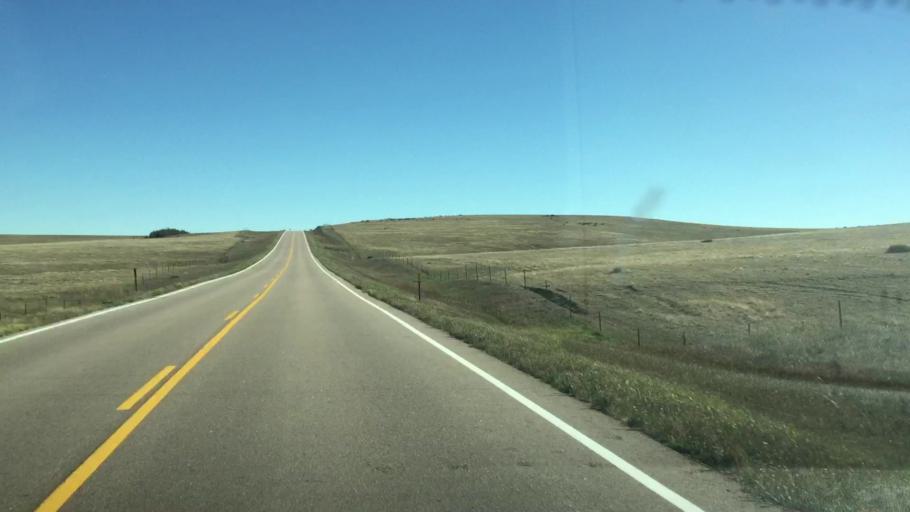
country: US
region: Colorado
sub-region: Lincoln County
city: Limon
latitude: 39.2847
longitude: -103.9828
